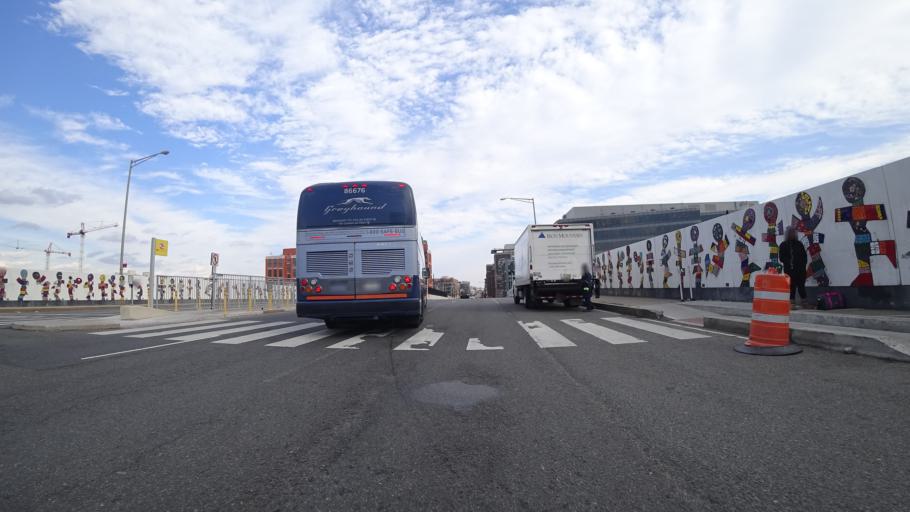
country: US
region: Washington, D.C.
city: Washington, D.C.
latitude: 38.9001
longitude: -77.0056
